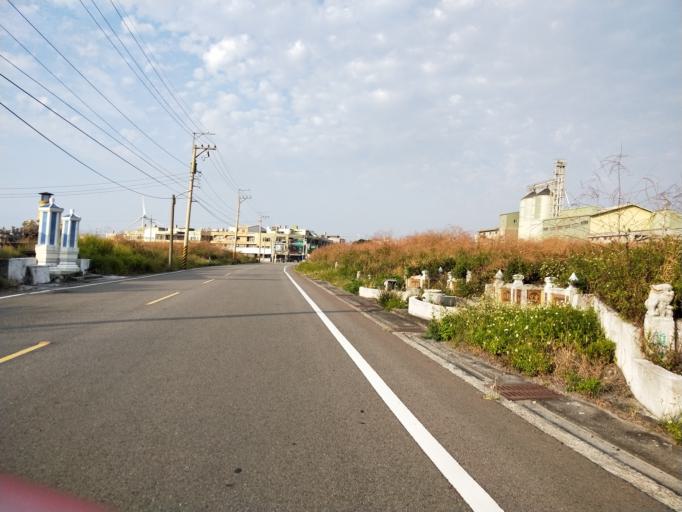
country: TW
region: Taiwan
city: Fengyuan
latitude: 24.3776
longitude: 120.5854
